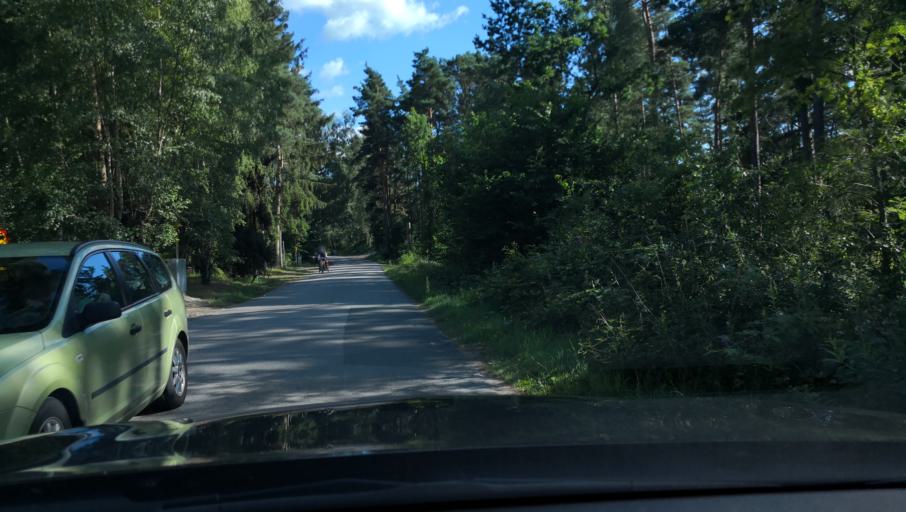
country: SE
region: Skane
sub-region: Simrishamns Kommun
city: Kivik
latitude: 55.7781
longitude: 14.1945
